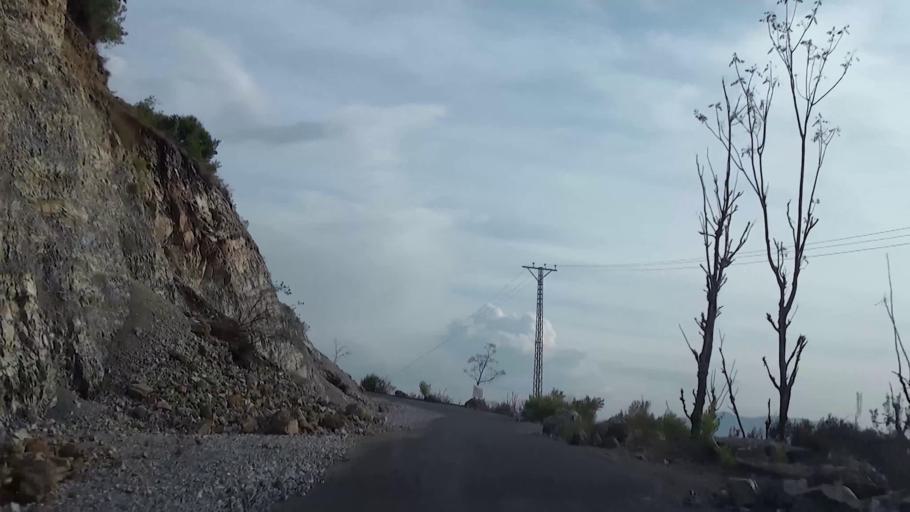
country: PK
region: Azad Kashmir
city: Muzaffarabad
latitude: 34.3619
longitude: 73.5065
